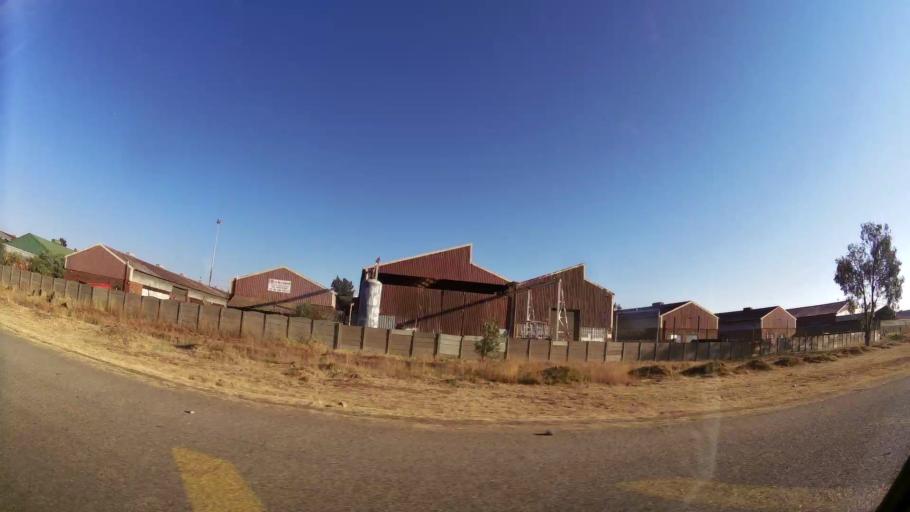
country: ZA
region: Gauteng
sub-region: Ekurhuleni Metropolitan Municipality
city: Germiston
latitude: -26.3530
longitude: 28.1237
